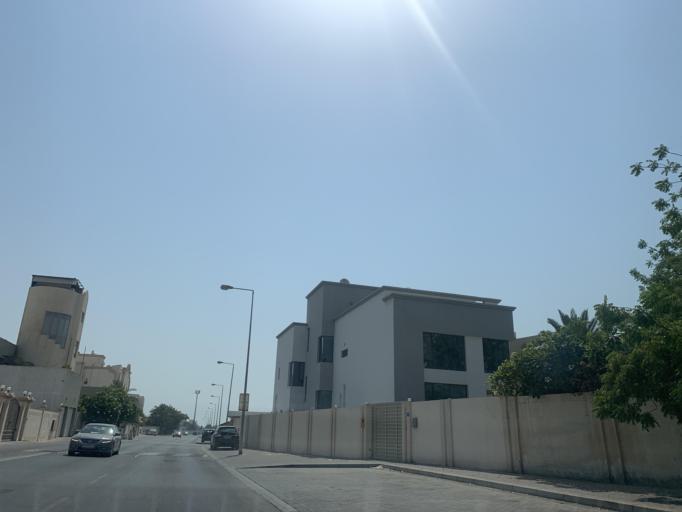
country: BH
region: Manama
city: Jidd Hafs
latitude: 26.2028
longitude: 50.5293
